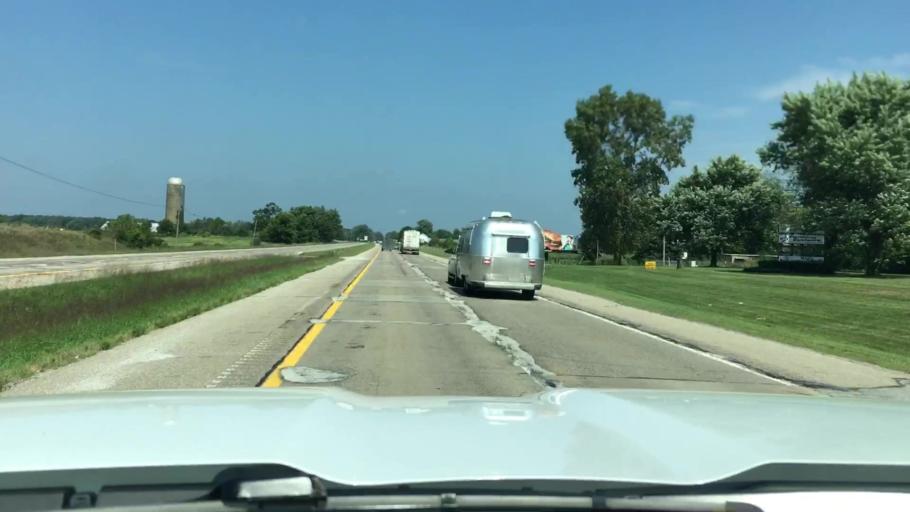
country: US
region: Michigan
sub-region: Kalamazoo County
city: Schoolcraft
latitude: 42.0979
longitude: -85.6368
